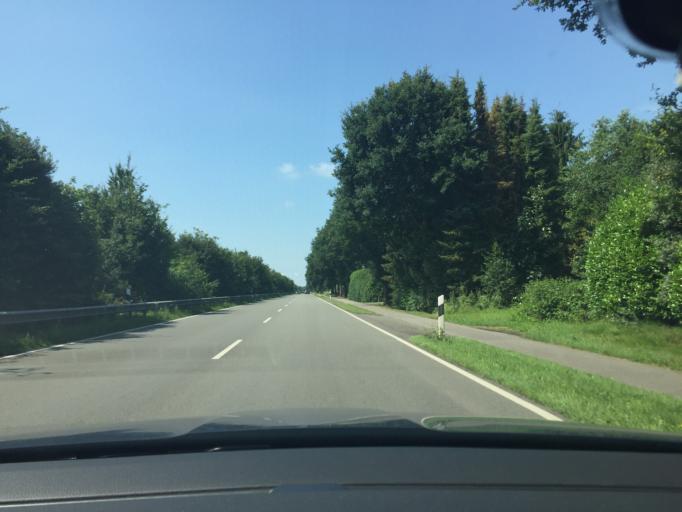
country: DE
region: Lower Saxony
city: Edewecht
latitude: 53.0891
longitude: 8.0235
